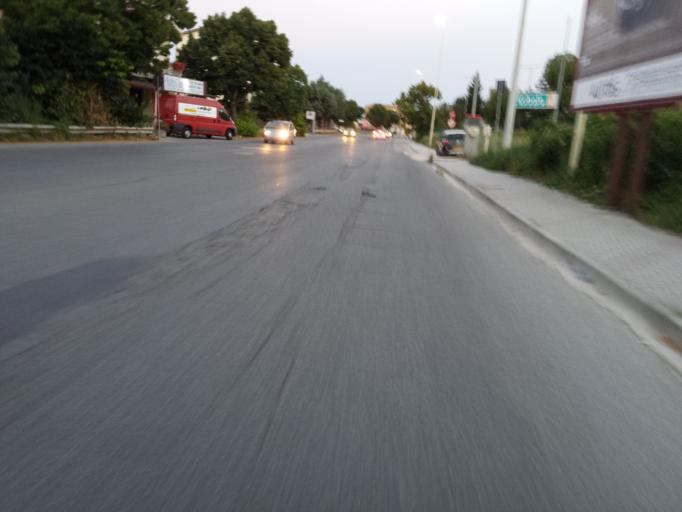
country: IT
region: Molise
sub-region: Provincia di Campobasso
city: Campobasso
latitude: 41.5831
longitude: 14.6734
